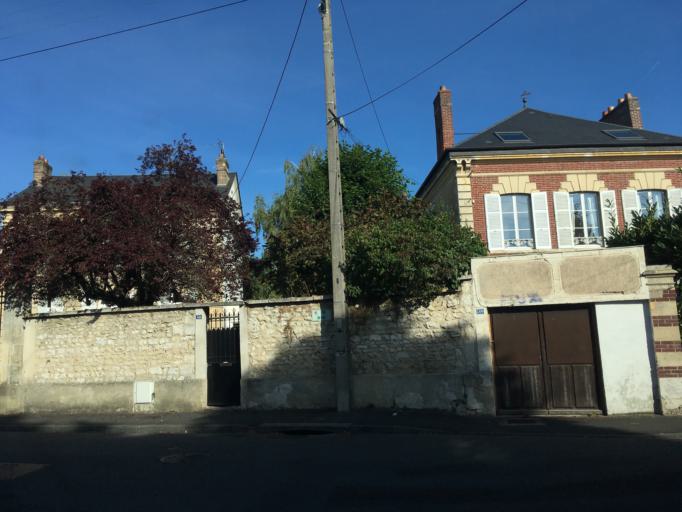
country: FR
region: Haute-Normandie
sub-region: Departement de l'Eure
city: Vernon
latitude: 49.0887
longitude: 1.4748
